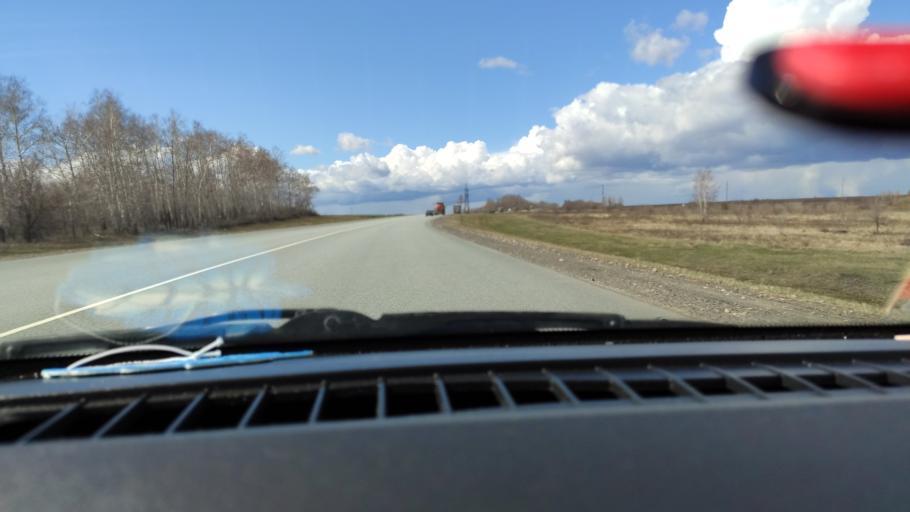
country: RU
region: Samara
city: Obsharovka
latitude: 53.2117
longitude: 48.7765
